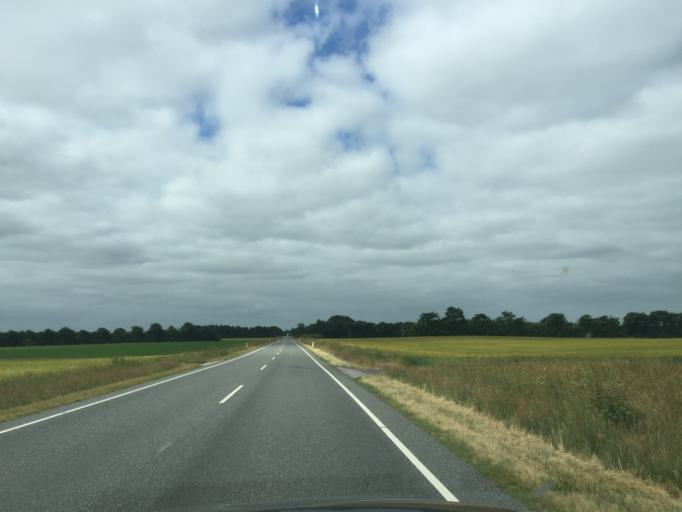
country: DK
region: South Denmark
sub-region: Vejen Kommune
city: Brorup
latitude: 55.4346
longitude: 8.9824
